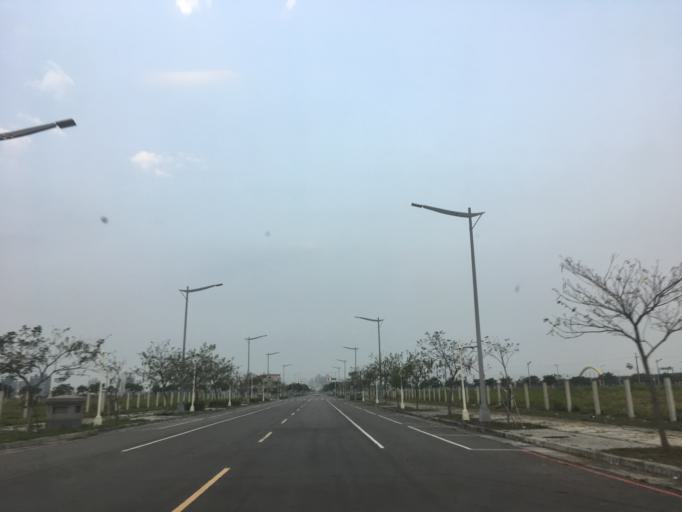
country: TW
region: Taiwan
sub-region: Taichung City
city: Taichung
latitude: 24.1979
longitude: 120.6783
